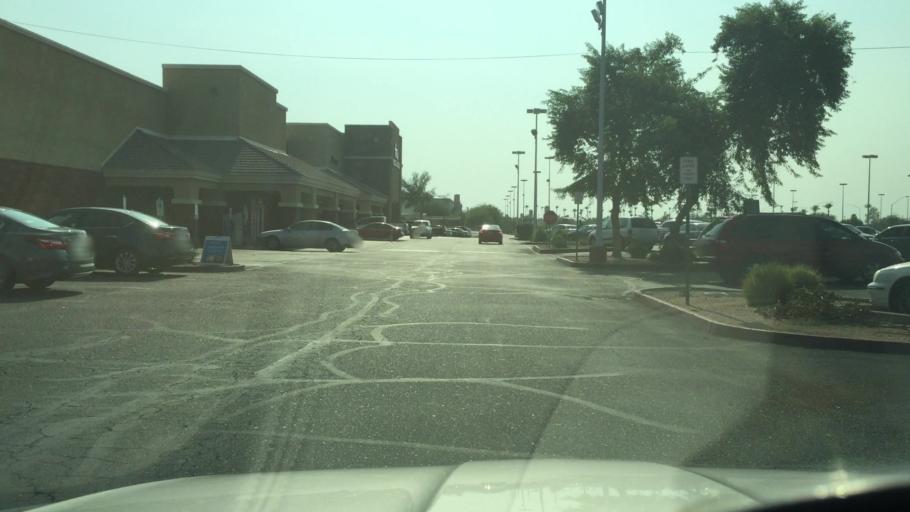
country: US
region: Arizona
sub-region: Maricopa County
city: Mesa
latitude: 33.4135
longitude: -111.8573
